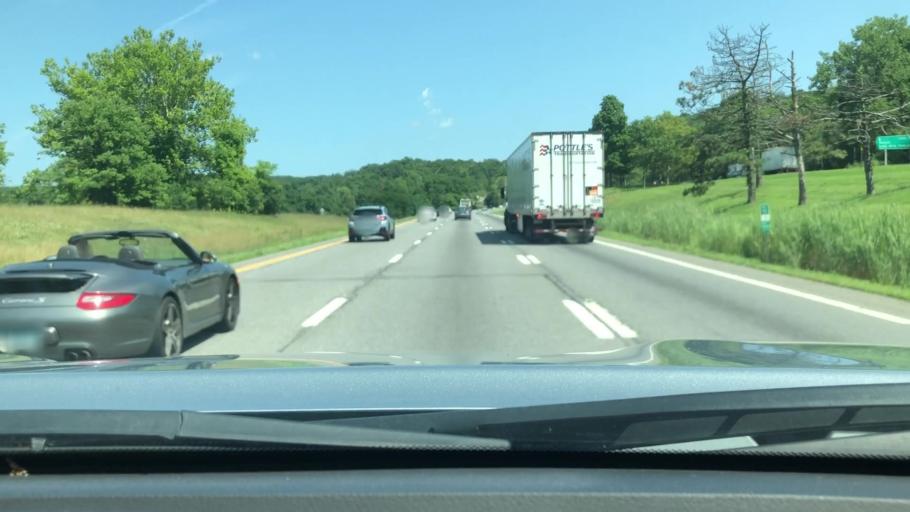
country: US
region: New York
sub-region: Dutchess County
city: Hillside Lake
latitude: 41.5473
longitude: -73.7255
